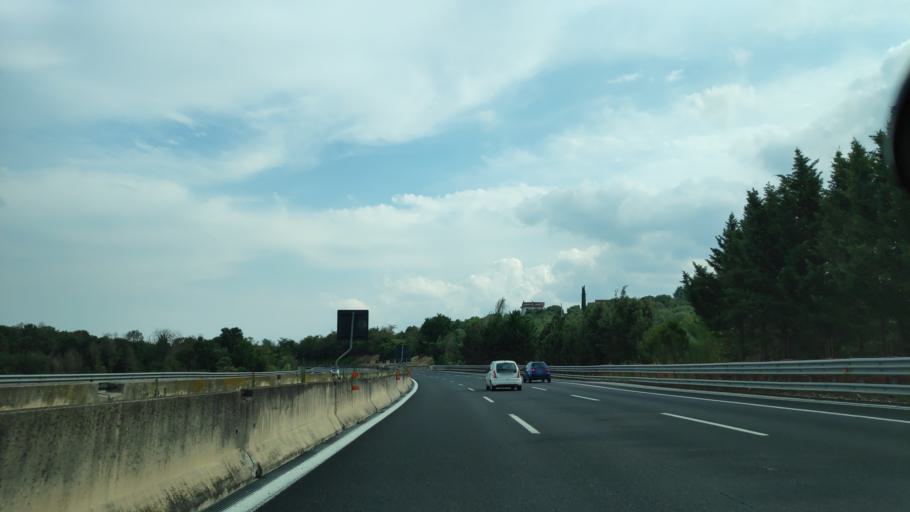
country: IT
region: Latium
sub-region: Citta metropolitana di Roma Capitale
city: Fiano Romano
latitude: 42.1822
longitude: 12.6022
